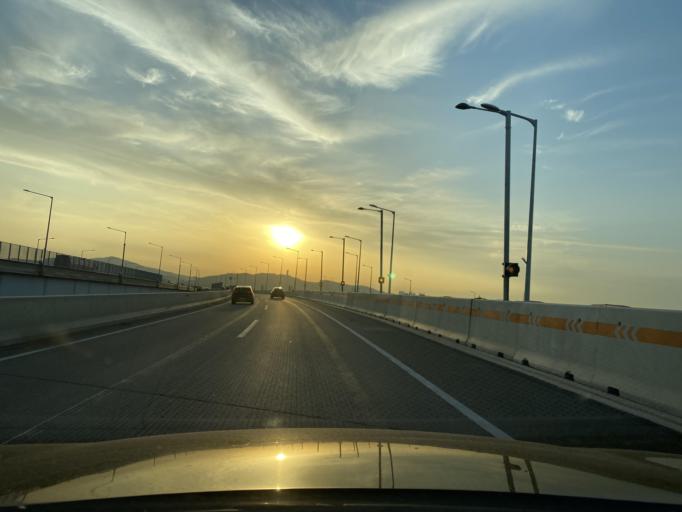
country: KR
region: Gyeonggi-do
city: Tongjin
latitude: 37.5404
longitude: 126.5667
